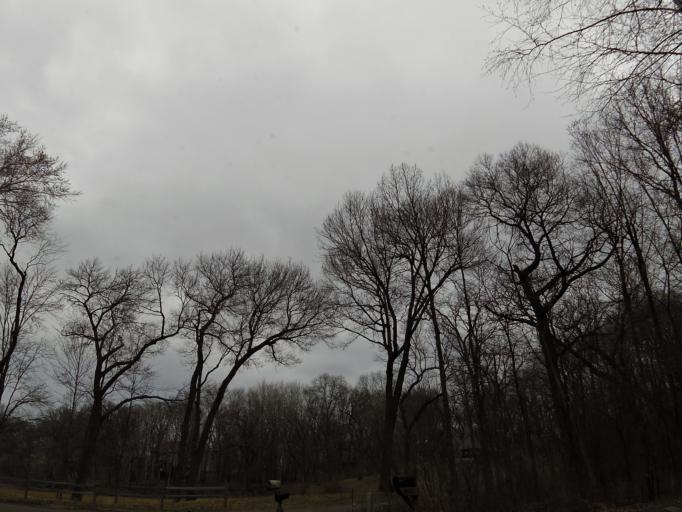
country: US
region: Minnesota
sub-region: Washington County
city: Lakeland
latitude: 44.9729
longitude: -92.7962
